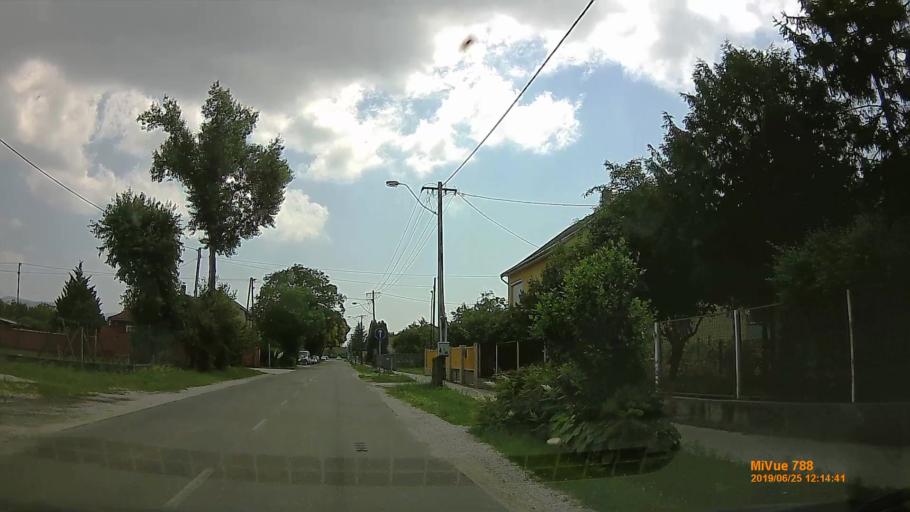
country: HU
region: Komarom-Esztergom
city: Dorog
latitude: 47.7392
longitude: 18.7231
